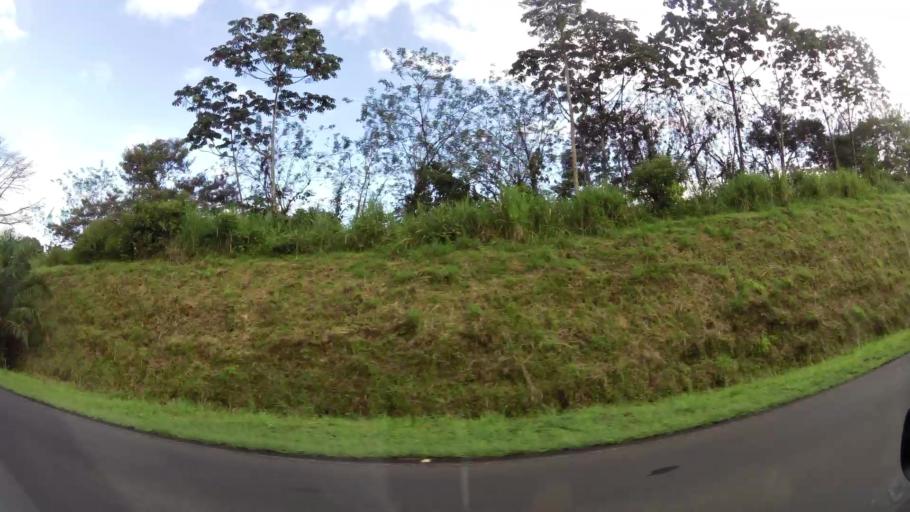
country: CR
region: Limon
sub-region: Canton de Guacimo
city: Guacimo
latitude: 10.1993
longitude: -83.6669
